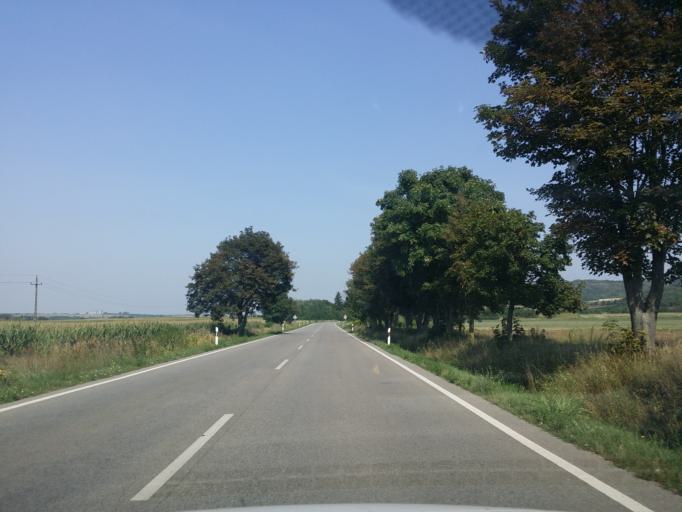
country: HU
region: Tolna
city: Simontornya
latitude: 46.7362
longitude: 18.5071
